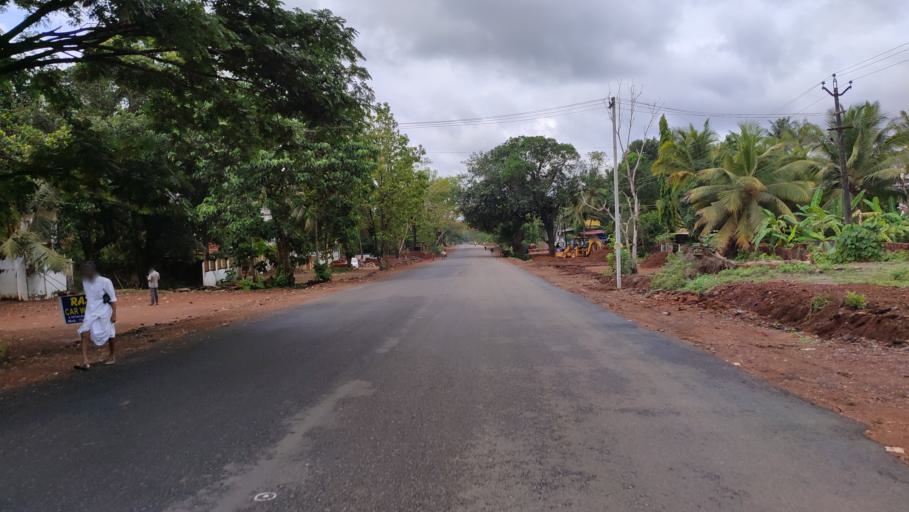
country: IN
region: Kerala
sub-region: Kasaragod District
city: Kasaragod
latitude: 12.5384
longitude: 75.0714
